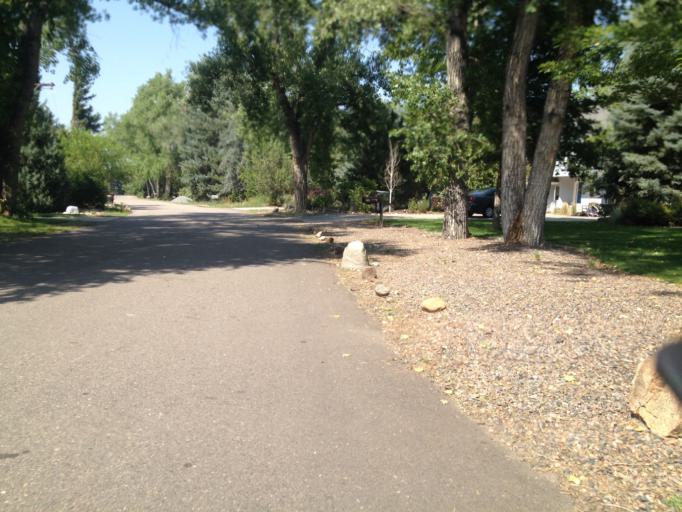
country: US
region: Colorado
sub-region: Boulder County
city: Boulder
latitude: 40.0015
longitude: -105.2145
